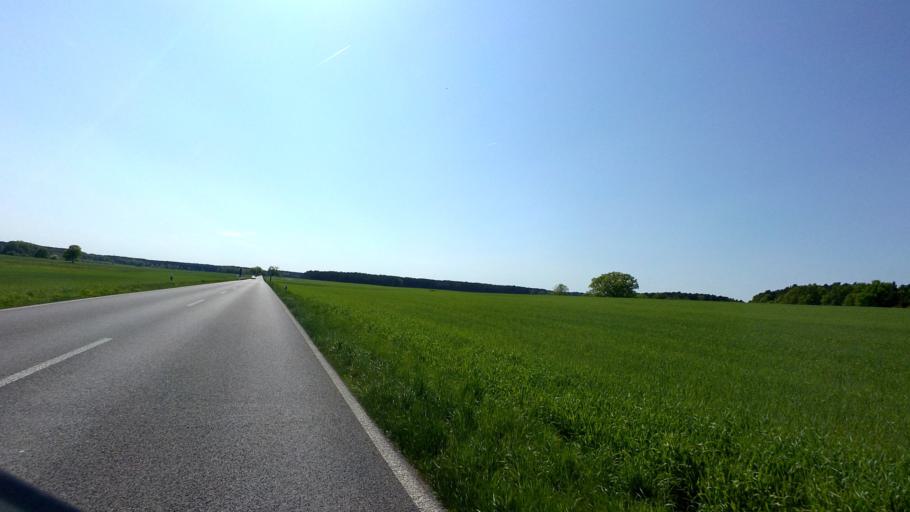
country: DE
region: Brandenburg
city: Tauche
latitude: 52.0612
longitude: 14.1408
